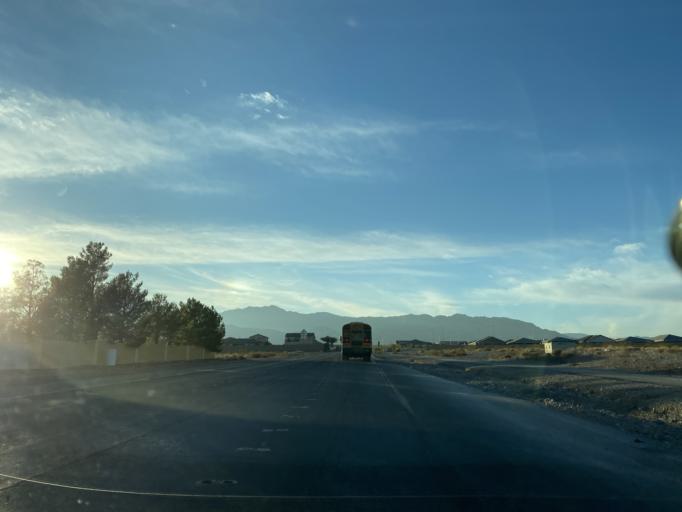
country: US
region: Nevada
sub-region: Clark County
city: Summerlin South
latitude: 36.2773
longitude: -115.3063
